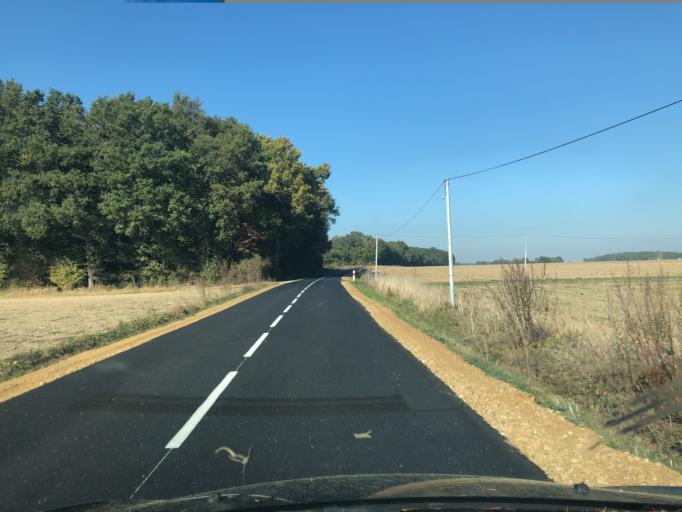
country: FR
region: Centre
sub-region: Departement d'Indre-et-Loire
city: Rouziers-de-Touraine
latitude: 47.5508
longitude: 0.6134
